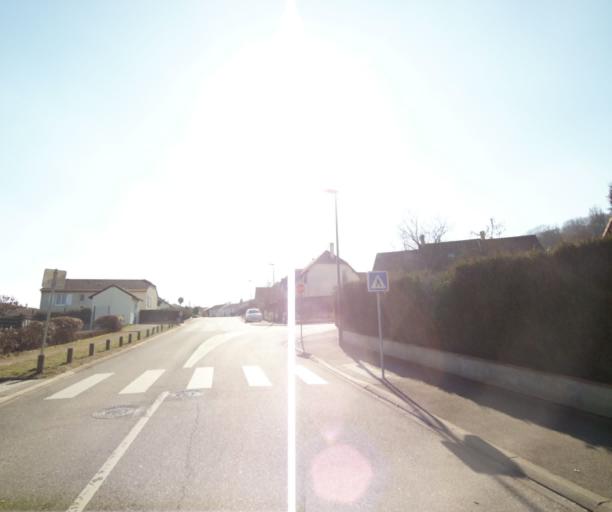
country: FR
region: Lorraine
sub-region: Departement de Meurthe-et-Moselle
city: Vandoeuvre-les-Nancy
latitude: 48.6419
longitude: 6.1770
